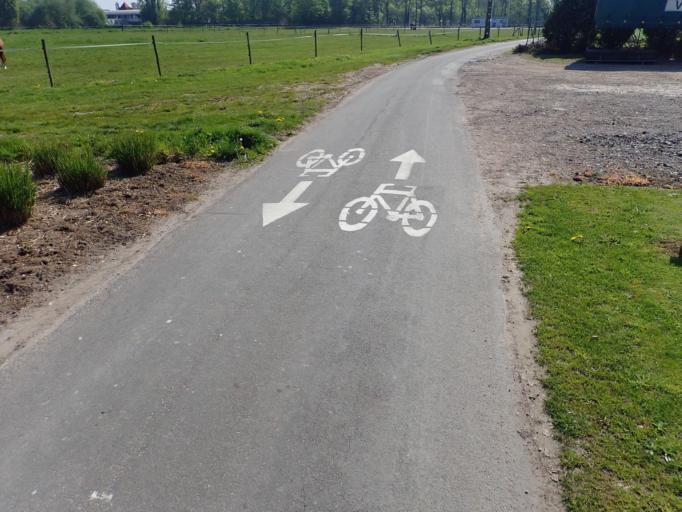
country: BE
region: Flanders
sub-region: Provincie Antwerpen
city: Sint-Katelijne-Waver
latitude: 51.0561
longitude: 4.5397
